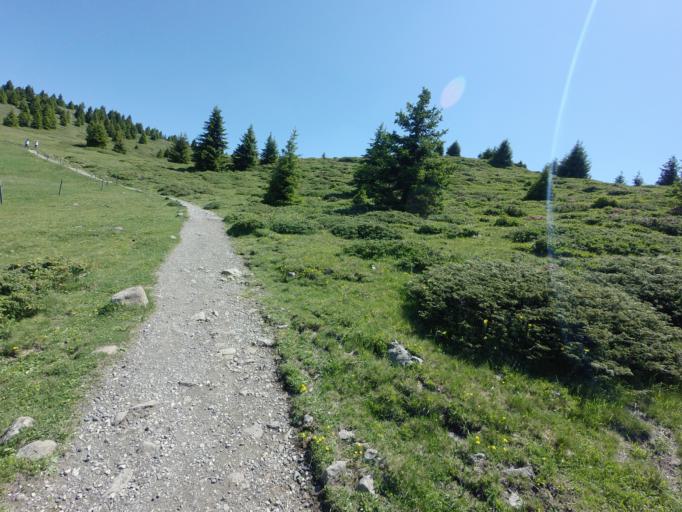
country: IT
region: Trentino-Alto Adige
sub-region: Bolzano
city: Castelrotto
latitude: 46.5606
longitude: 11.6078
